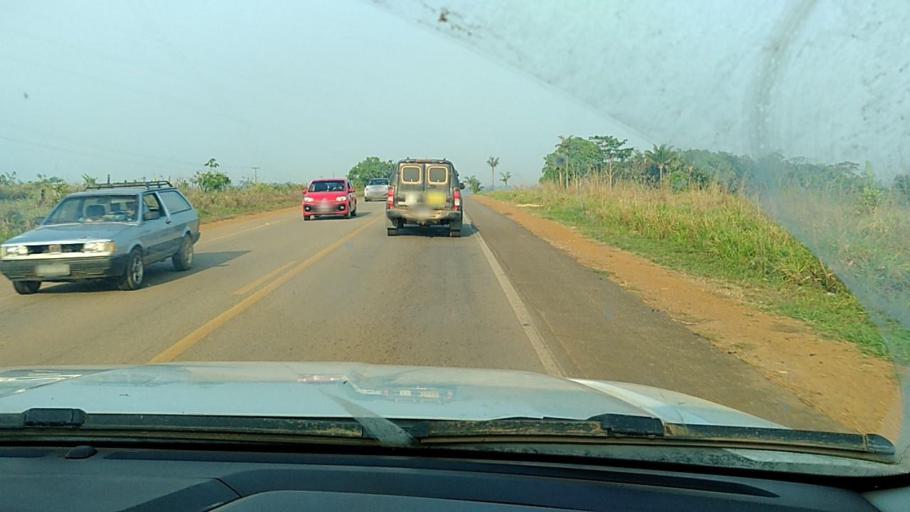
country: BR
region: Rondonia
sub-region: Porto Velho
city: Porto Velho
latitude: -8.7414
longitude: -63.9418
